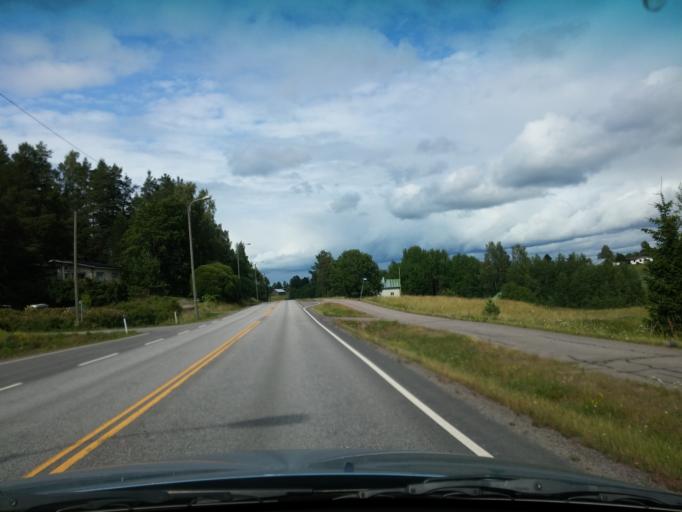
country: FI
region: Uusimaa
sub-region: Porvoo
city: Askola
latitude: 60.5139
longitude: 25.5777
